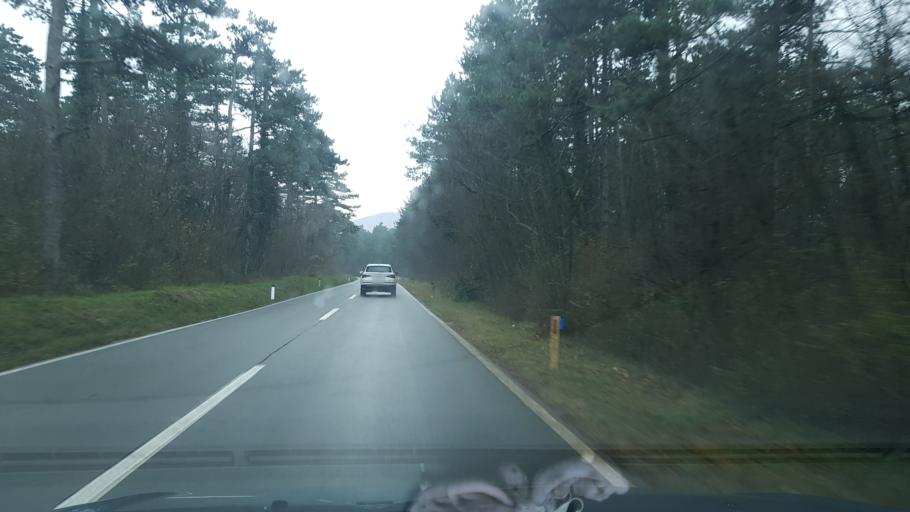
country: SI
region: Sezana
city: Sezana
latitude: 45.7316
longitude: 13.8673
